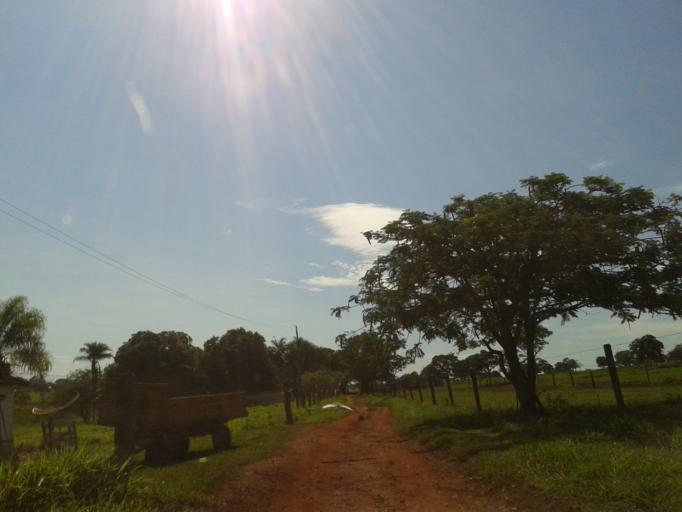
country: BR
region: Minas Gerais
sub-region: Santa Vitoria
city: Santa Vitoria
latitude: -19.1013
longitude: -50.5086
